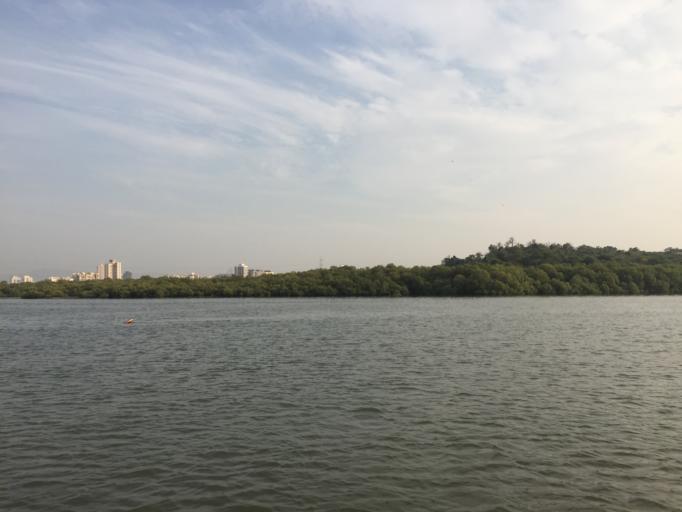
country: IN
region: Maharashtra
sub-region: Mumbai Suburban
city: Borivli
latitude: 19.2250
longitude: 72.8123
